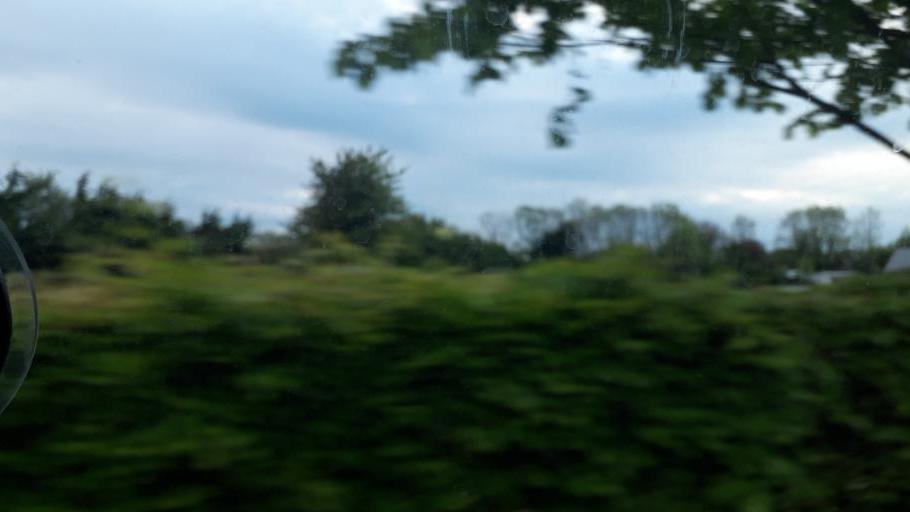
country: IE
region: Leinster
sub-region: Kildare
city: Celbridge
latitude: 53.3213
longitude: -6.5491
